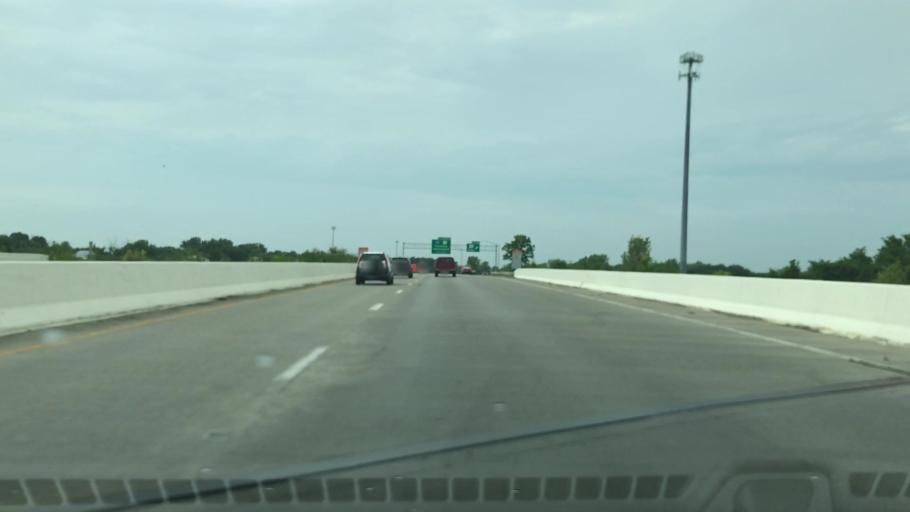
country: US
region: Ohio
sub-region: Clark County
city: Holiday Valley
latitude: 39.8403
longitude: -83.9922
